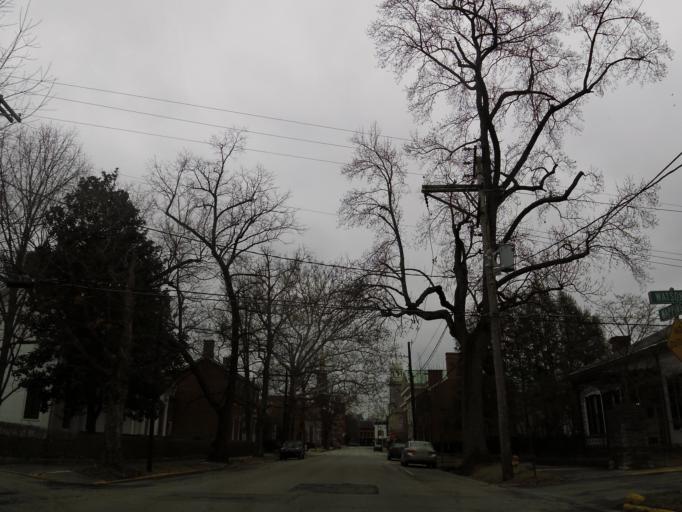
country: US
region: Kentucky
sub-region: Franklin County
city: Frankfort
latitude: 38.1985
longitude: -84.8811
